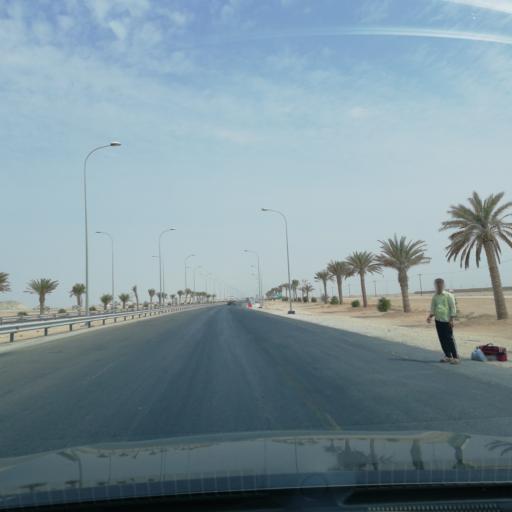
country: OM
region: Zufar
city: Salalah
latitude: 17.6140
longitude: 54.0321
